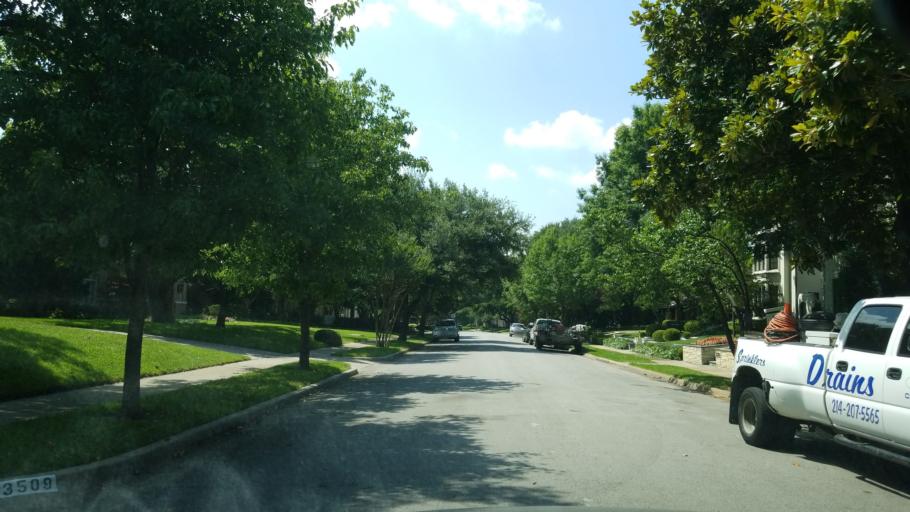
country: US
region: Texas
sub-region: Dallas County
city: Highland Park
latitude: 32.8267
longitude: -96.7907
